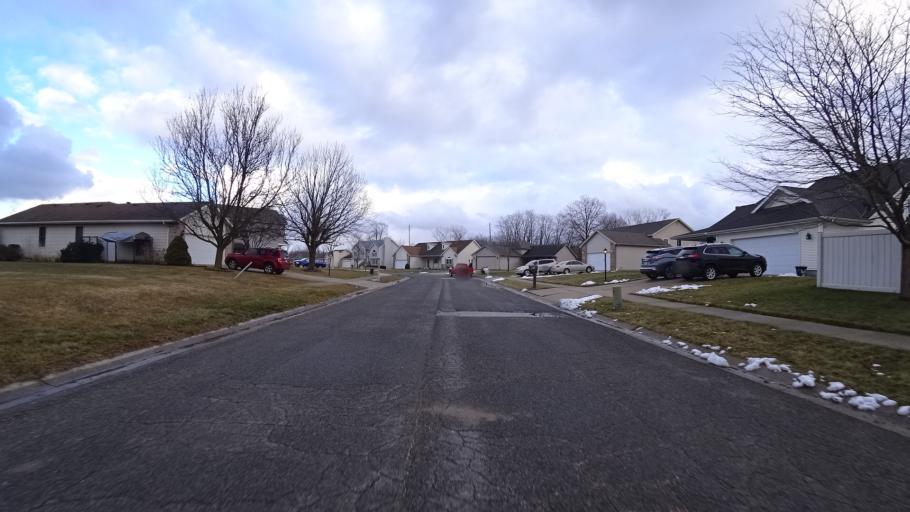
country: US
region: Indiana
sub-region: Porter County
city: Porter
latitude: 41.6174
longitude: -87.0841
